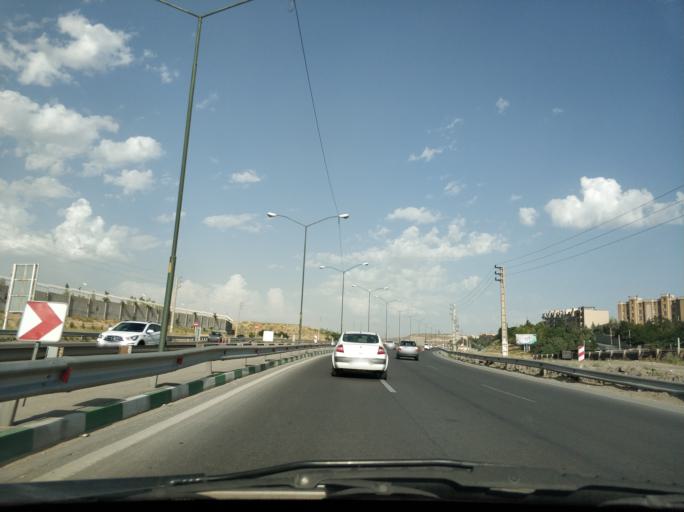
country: IR
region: Tehran
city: Tajrish
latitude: 35.7481
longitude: 51.5935
